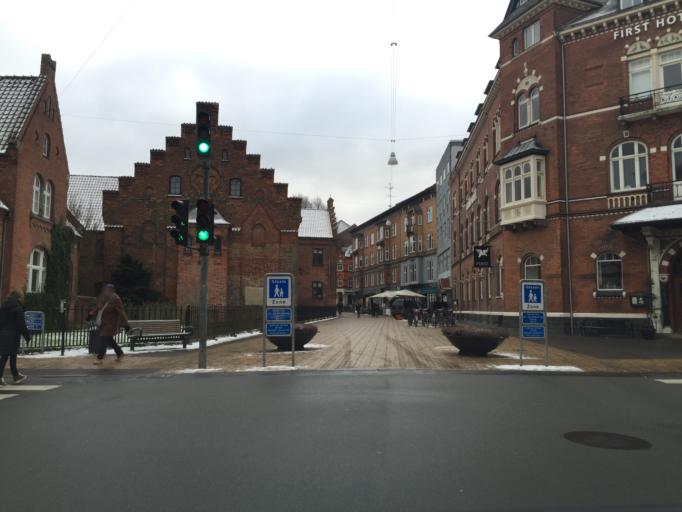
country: DK
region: South Denmark
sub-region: Odense Kommune
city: Odense
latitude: 55.3975
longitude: 10.3851
